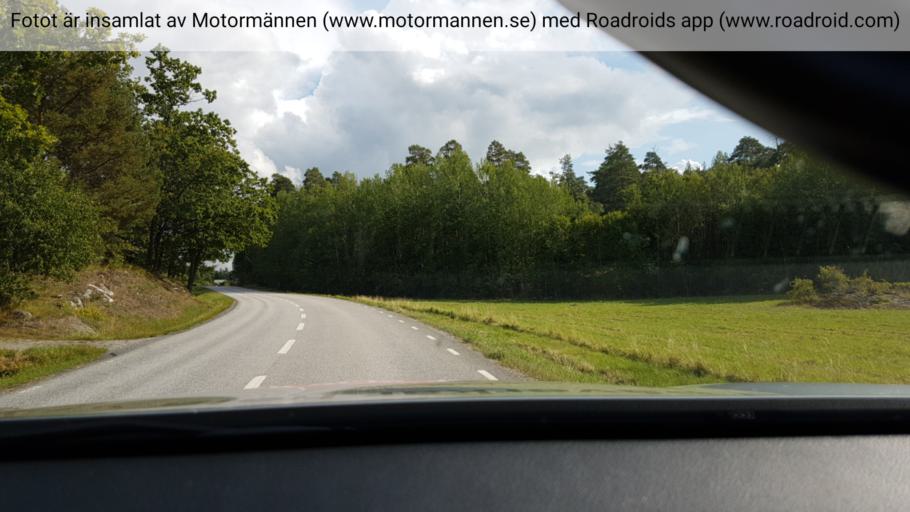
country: SE
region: Stockholm
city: Stenhamra
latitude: 59.3851
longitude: 17.6836
